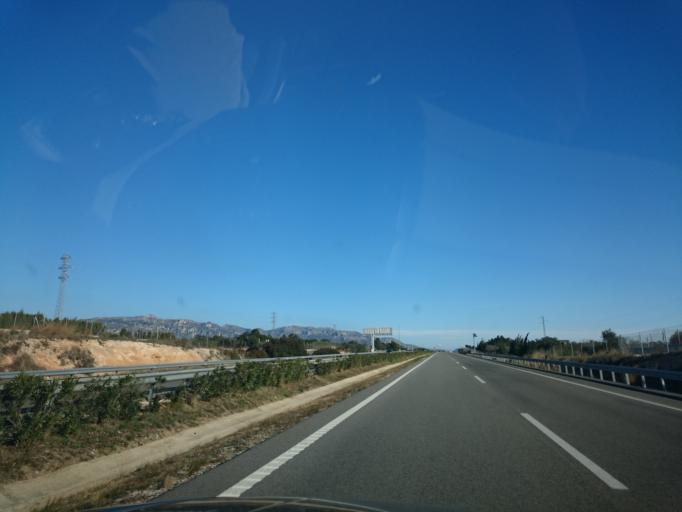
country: ES
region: Catalonia
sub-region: Provincia de Tarragona
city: l'Ametlla de Mar
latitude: 40.8911
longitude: 0.8038
